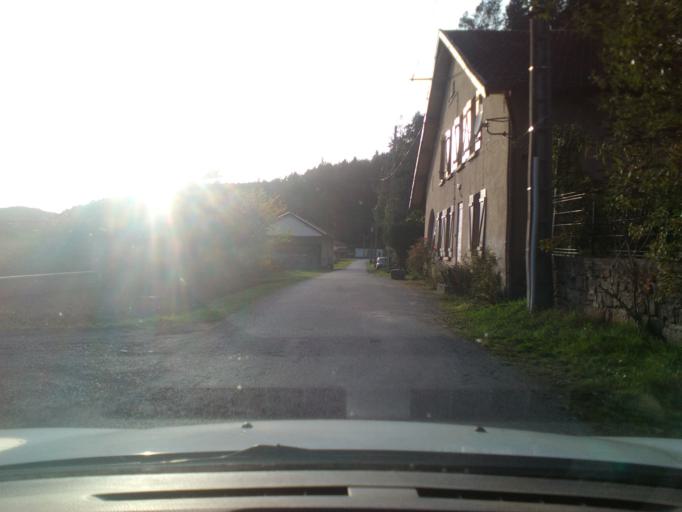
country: FR
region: Lorraine
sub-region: Departement des Vosges
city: Bruyeres
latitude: 48.2623
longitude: 6.7986
